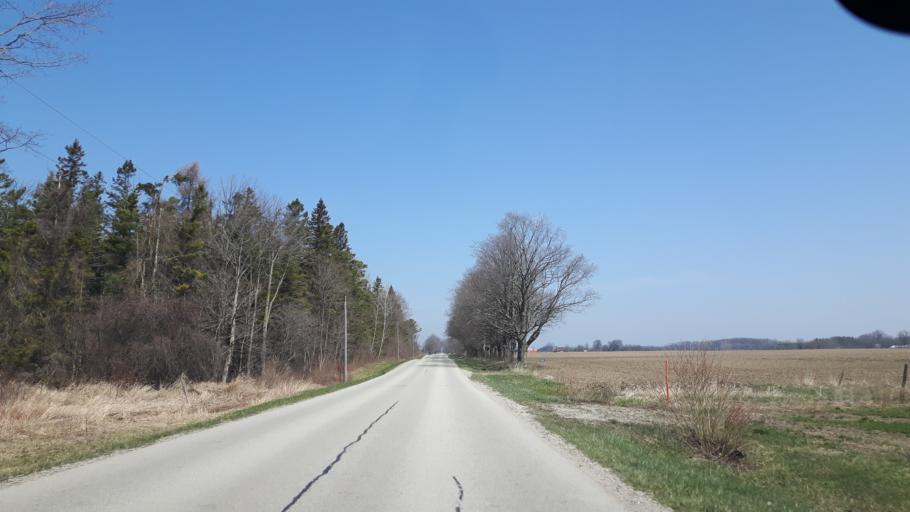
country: CA
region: Ontario
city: Goderich
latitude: 43.6313
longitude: -81.6846
